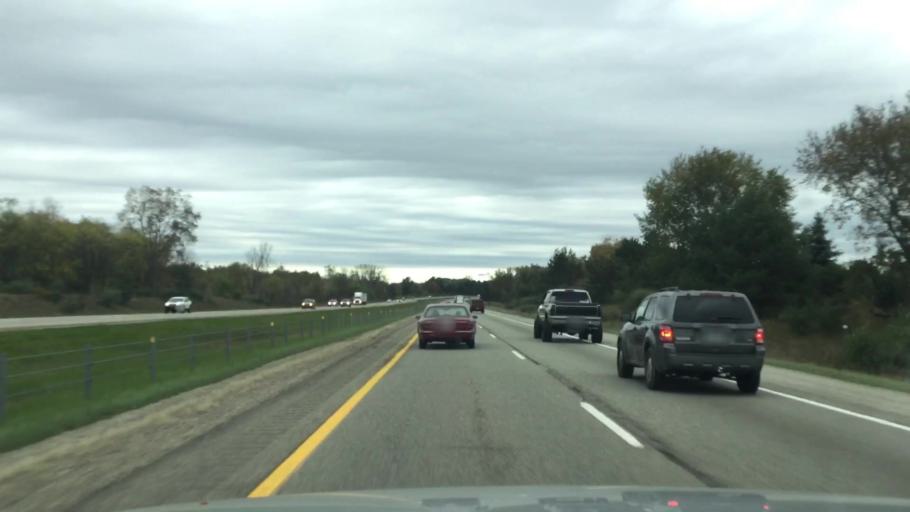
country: US
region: Michigan
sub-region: Livingston County
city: Brighton
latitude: 42.5871
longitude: -83.7385
